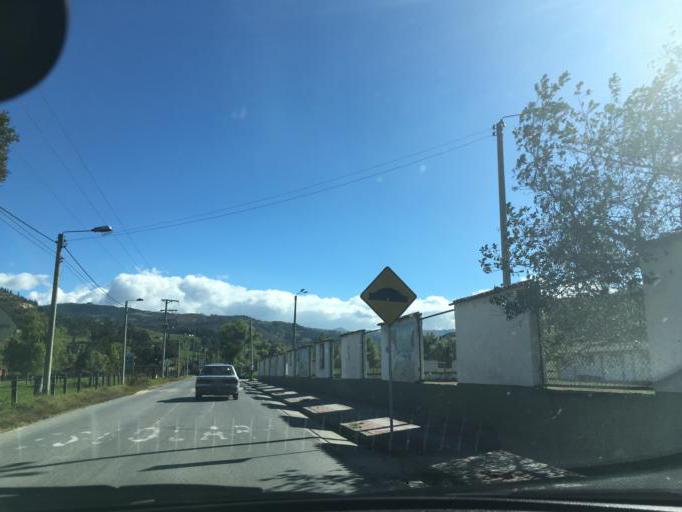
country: CO
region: Boyaca
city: Firavitoba
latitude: 5.6078
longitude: -72.9800
